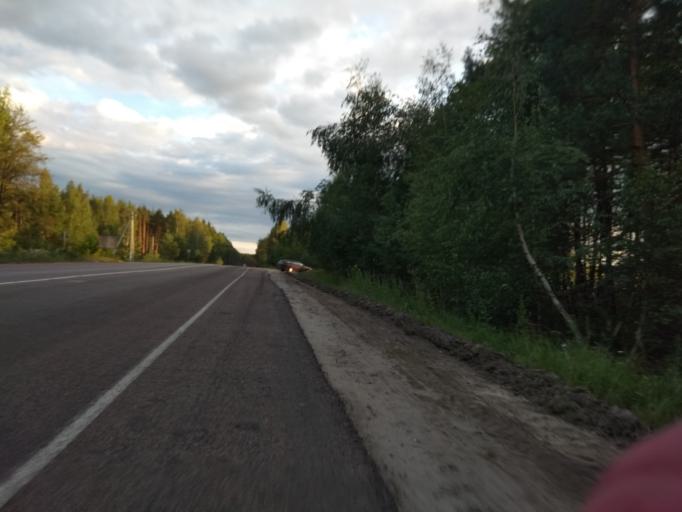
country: RU
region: Moskovskaya
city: Misheronskiy
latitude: 55.6341
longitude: 39.7463
